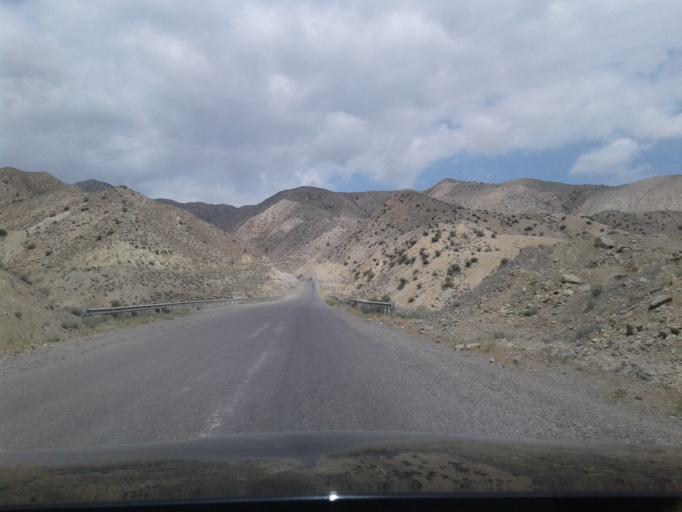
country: TM
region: Ahal
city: Baharly
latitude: 38.5049
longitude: 57.0633
